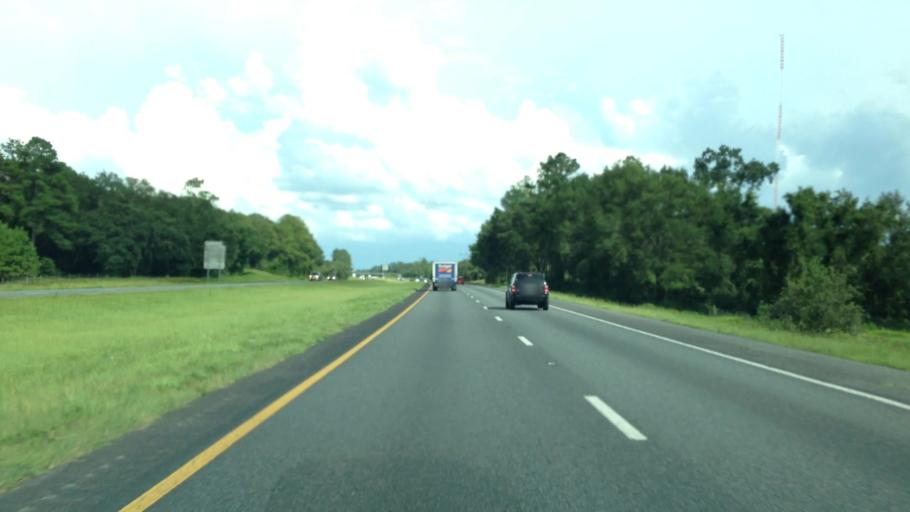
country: US
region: Florida
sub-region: Suwannee County
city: Live Oak
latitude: 30.3182
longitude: -82.9459
